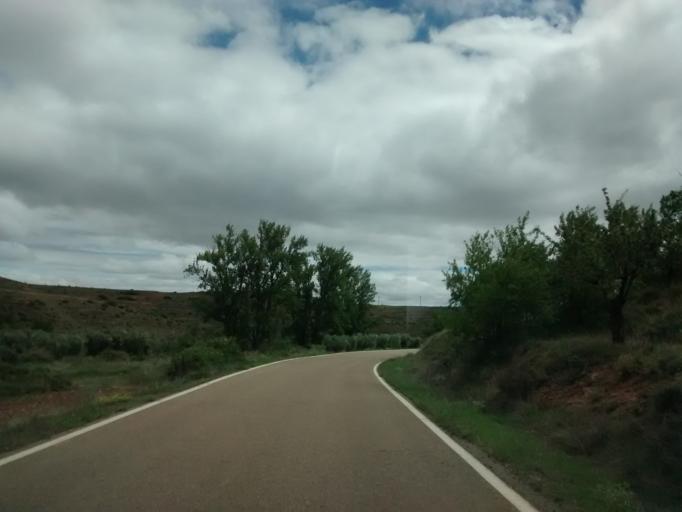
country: ES
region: Aragon
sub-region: Provincia de Zaragoza
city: Lituenigo
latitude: 41.8395
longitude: -1.7465
